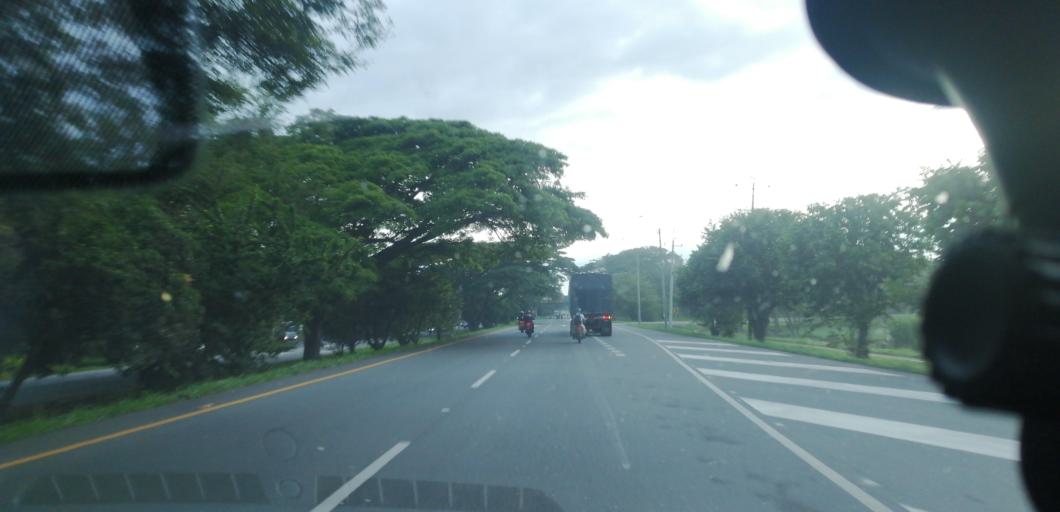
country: CO
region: Valle del Cauca
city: Palmira
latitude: 3.5237
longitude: -76.3407
